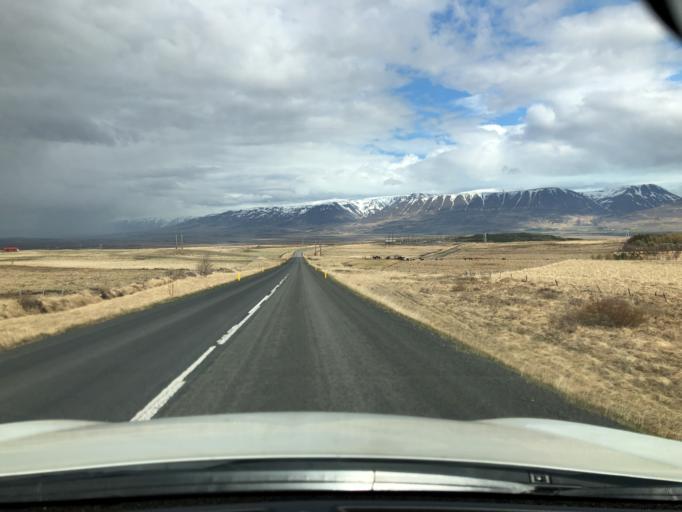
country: IS
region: Northwest
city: Saudarkrokur
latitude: 65.5430
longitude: -19.4985
